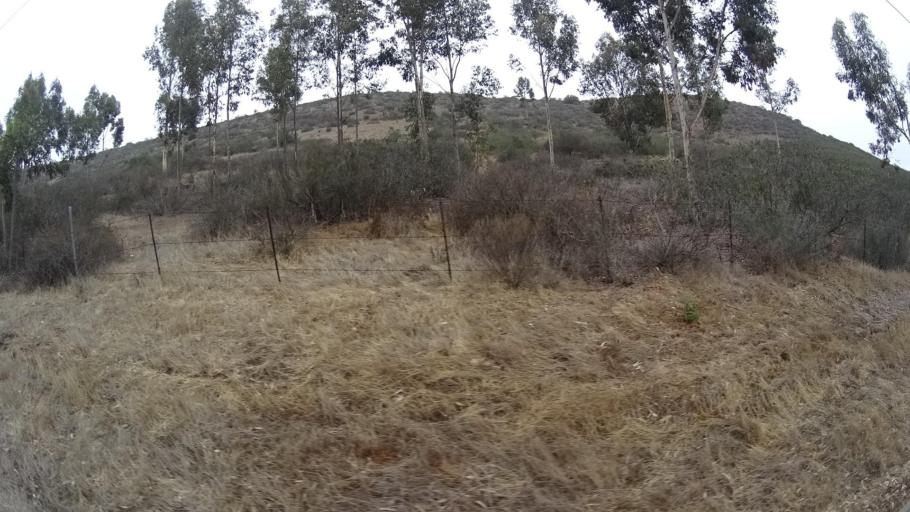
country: US
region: California
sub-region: San Diego County
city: Poway
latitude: 32.9418
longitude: -116.9974
